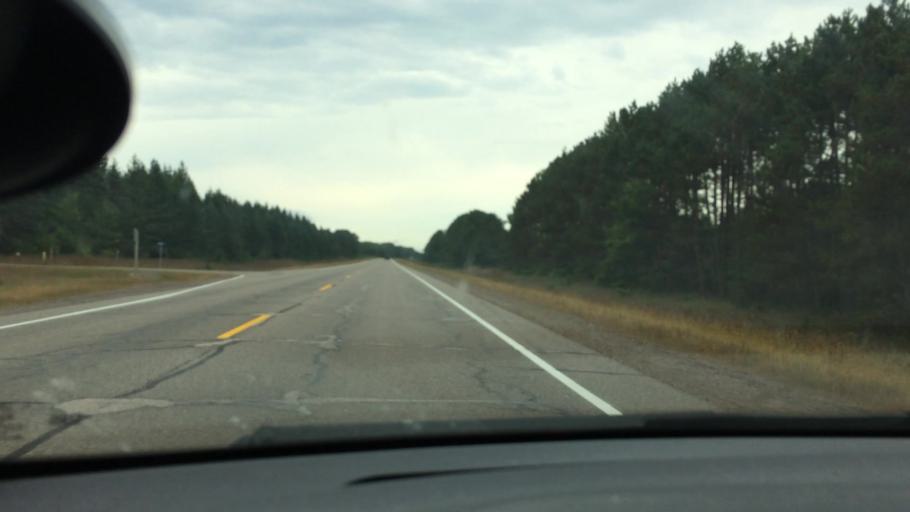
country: US
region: Wisconsin
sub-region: Eau Claire County
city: Augusta
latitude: 44.5807
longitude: -91.0692
